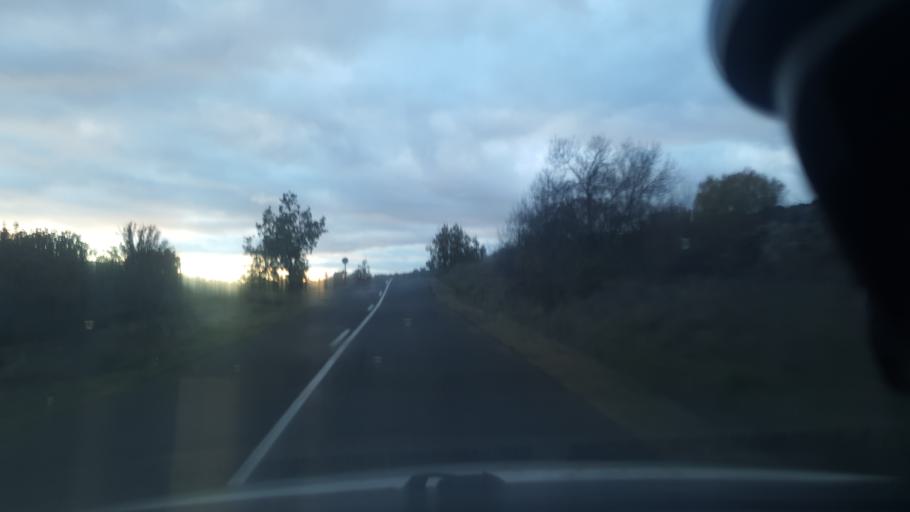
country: ES
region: Castille and Leon
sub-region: Provincia de Segovia
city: Vegas de Matute
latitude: 40.7240
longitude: -4.2943
